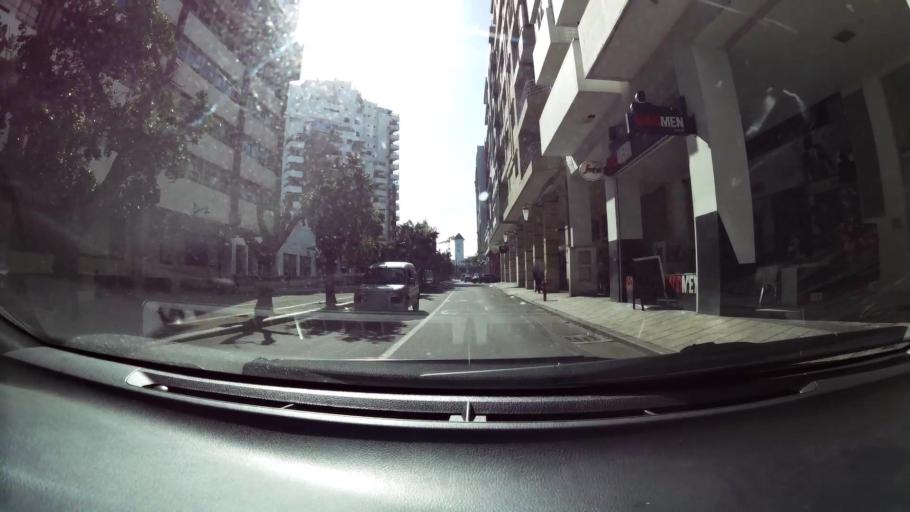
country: MA
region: Grand Casablanca
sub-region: Casablanca
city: Casablanca
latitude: 33.5914
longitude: -7.5940
